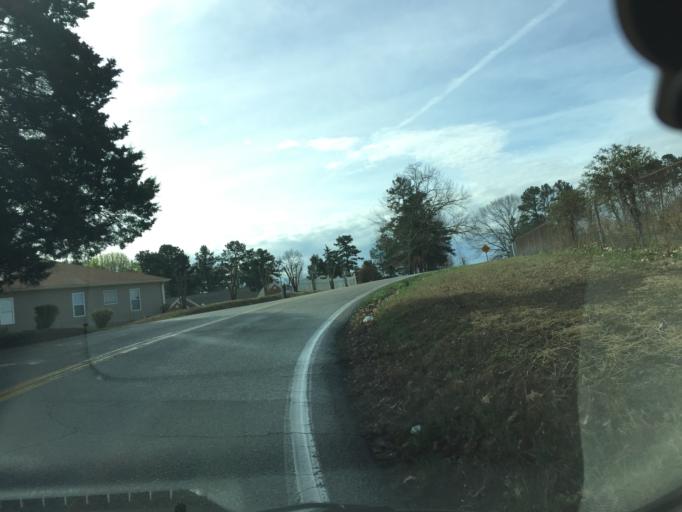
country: US
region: Tennessee
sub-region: Hamilton County
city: Collegedale
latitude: 35.0569
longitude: -85.0997
